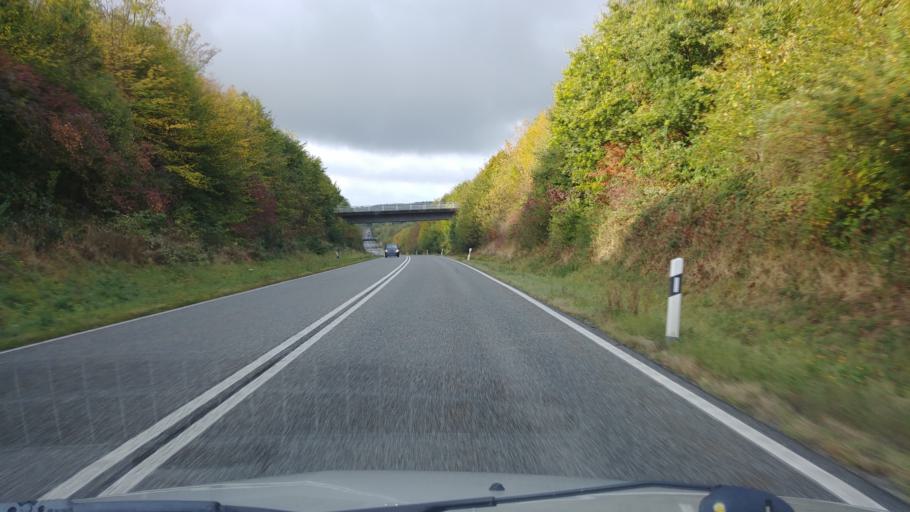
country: DE
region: Rheinland-Pfalz
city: Lautzenhausen
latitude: 49.9256
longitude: 7.2676
